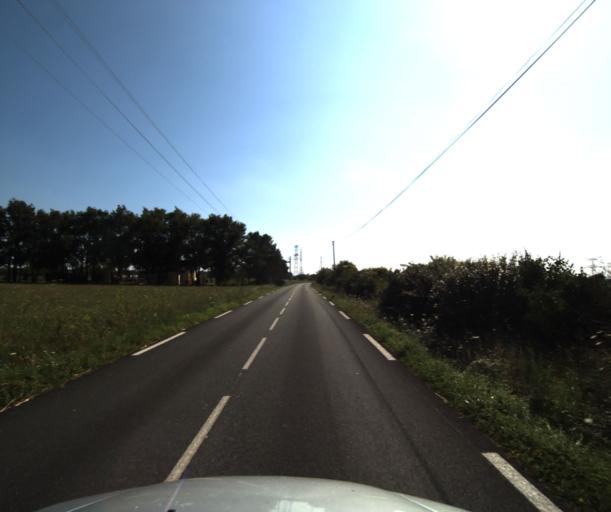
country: FR
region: Midi-Pyrenees
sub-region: Departement de la Haute-Garonne
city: Lacasse
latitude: 43.3849
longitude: 1.2479
